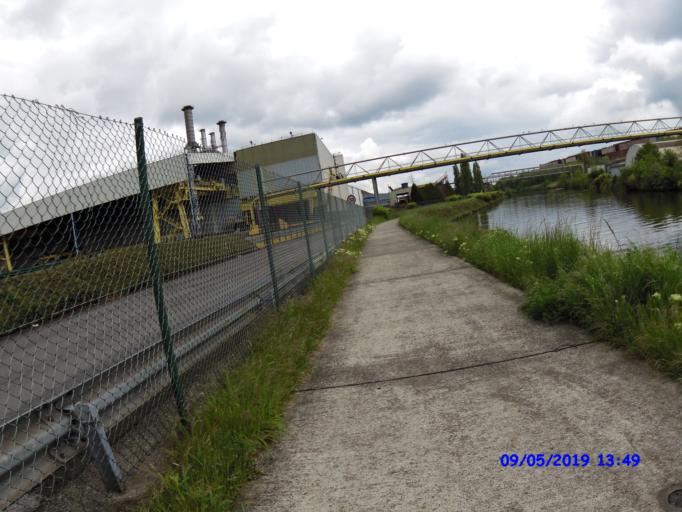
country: BE
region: Wallonia
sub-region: Province du Hainaut
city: Chatelet
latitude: 50.4107
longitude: 4.5270
